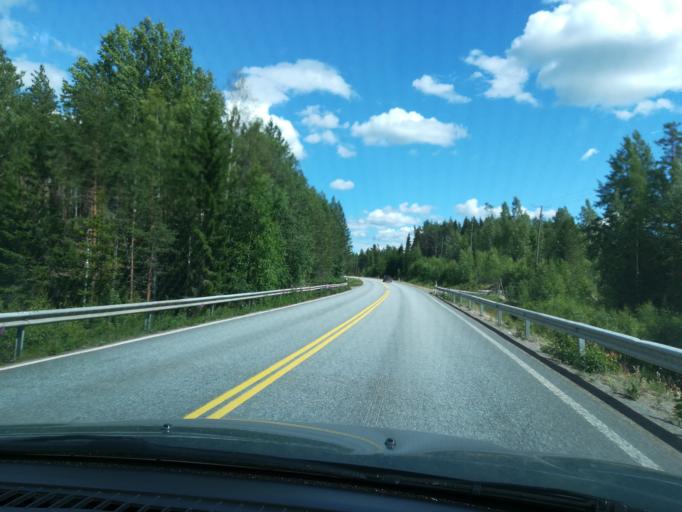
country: FI
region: Southern Savonia
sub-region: Mikkeli
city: Hirvensalmi
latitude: 61.6590
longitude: 26.9415
